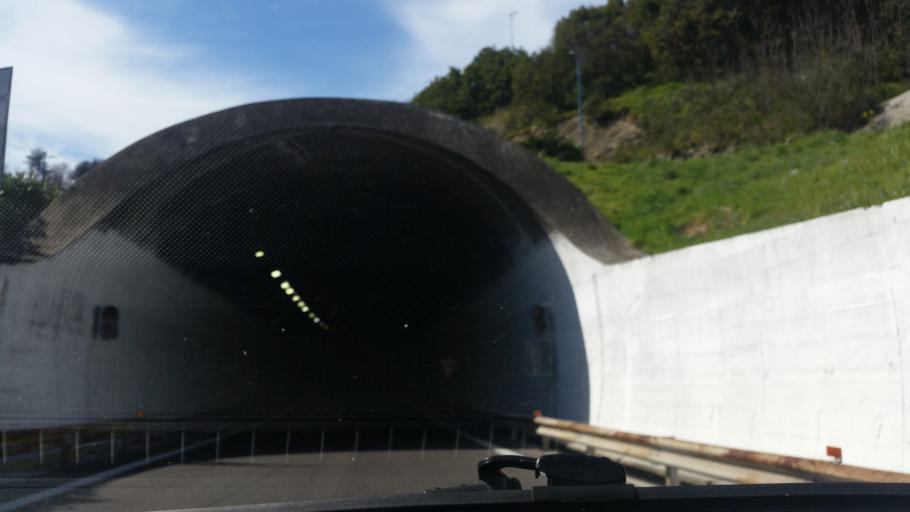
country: IT
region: Campania
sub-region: Provincia di Napoli
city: Napoli
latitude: 40.8625
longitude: 14.2348
